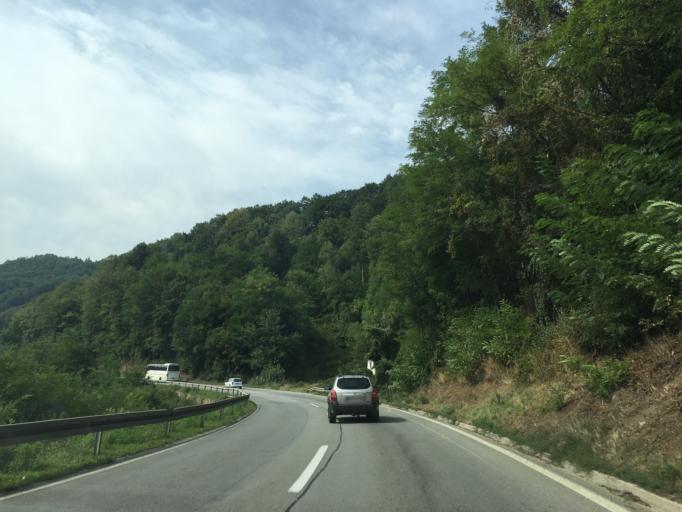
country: RS
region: Central Serbia
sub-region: Moravicki Okrug
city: Lucani
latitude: 43.8831
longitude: 20.1136
